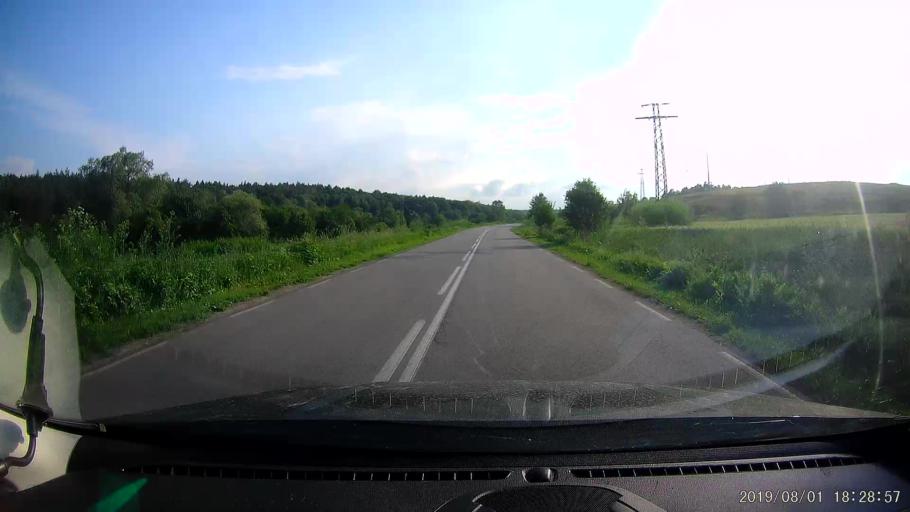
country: BG
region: Shumen
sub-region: Obshtina Venets
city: Venets
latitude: 43.5683
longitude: 26.9525
